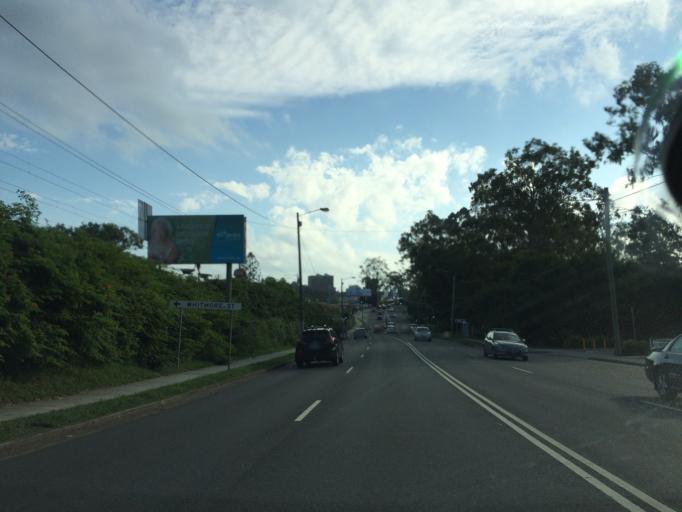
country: AU
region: Queensland
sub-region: Brisbane
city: Toowong
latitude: -27.4894
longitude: 152.9879
